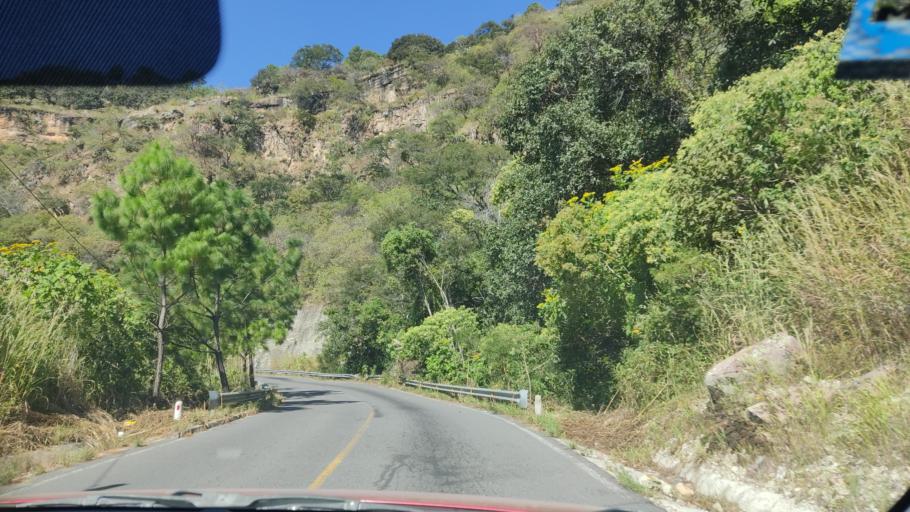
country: MX
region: Nayarit
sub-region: Jala
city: Rosa Blanca
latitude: 21.0898
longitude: -104.3780
